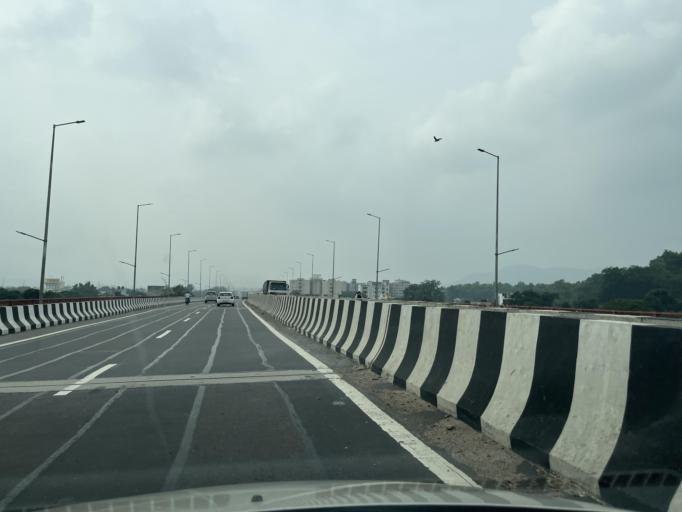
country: IN
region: Uttarakhand
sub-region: Dehradun
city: Raiwala
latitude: 30.0069
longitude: 78.1901
